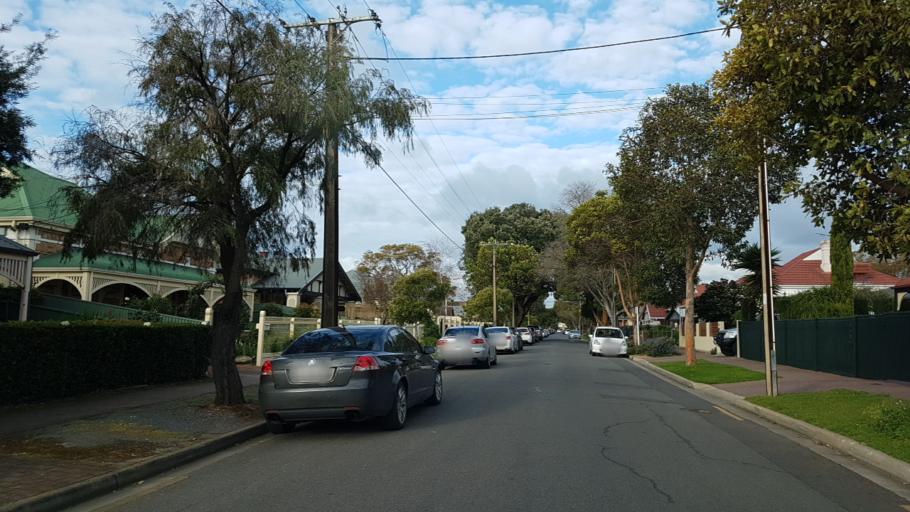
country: AU
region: South Australia
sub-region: Prospect
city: Prospect
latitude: -34.8881
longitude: 138.5976
